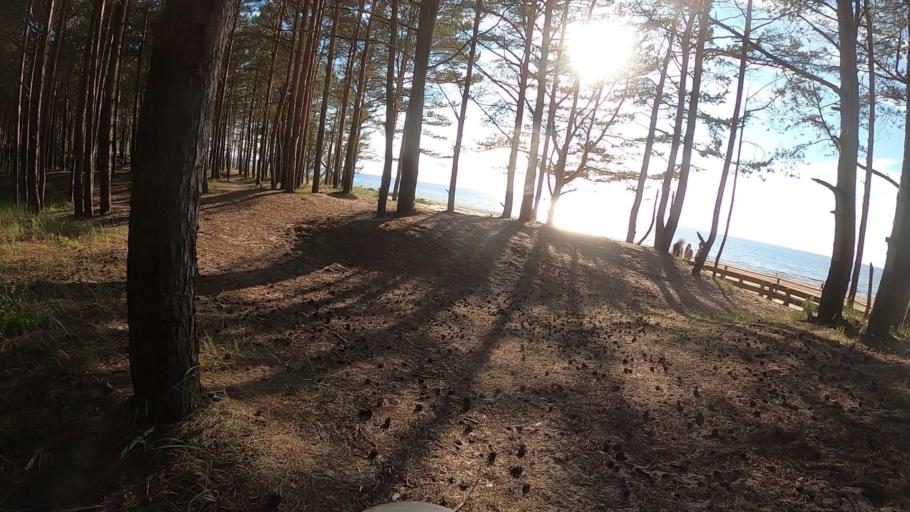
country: LV
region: Riga
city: Jaunciems
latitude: 57.1131
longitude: 24.1904
